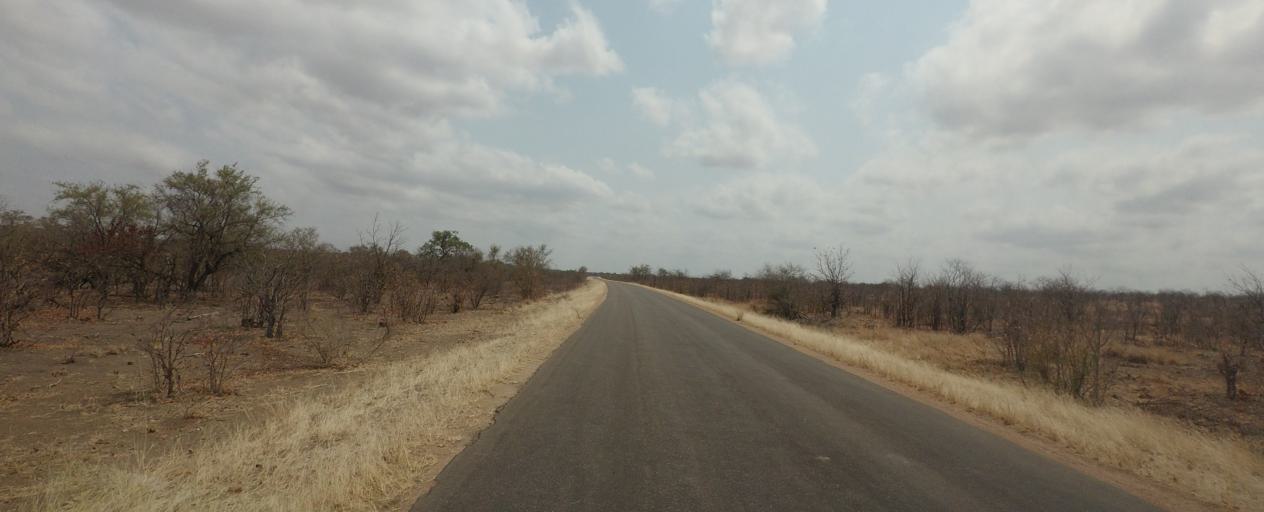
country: ZA
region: Limpopo
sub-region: Mopani District Municipality
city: Phalaborwa
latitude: -23.5932
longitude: 31.4539
